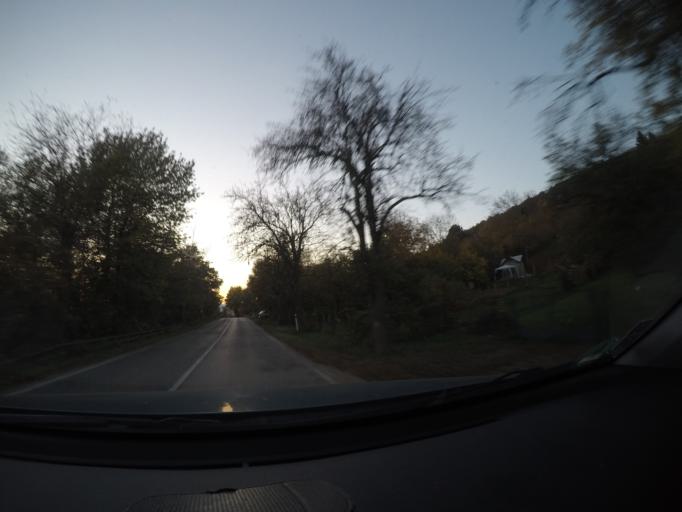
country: SK
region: Trenciansky
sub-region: Okres Trencin
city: Trencin
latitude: 48.9051
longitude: 18.0657
